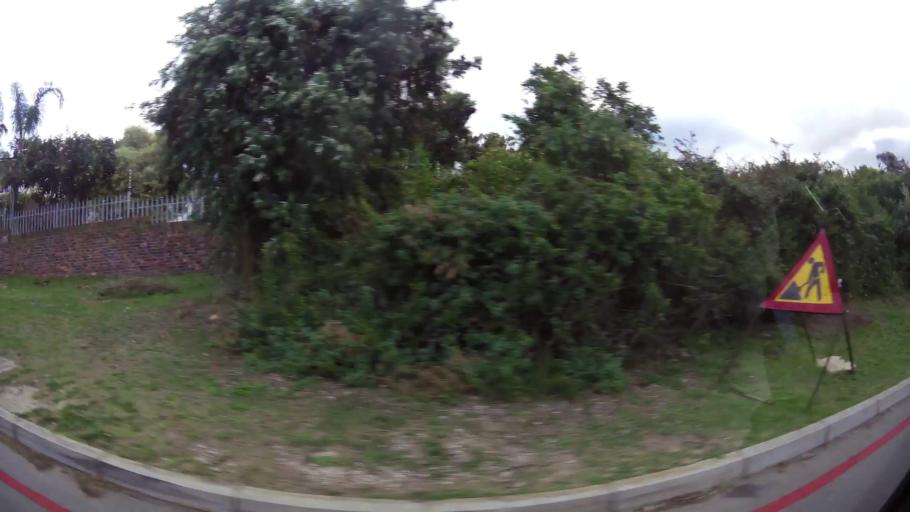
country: ZA
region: Western Cape
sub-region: Eden District Municipality
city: Plettenberg Bay
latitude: -34.0514
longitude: 23.3720
